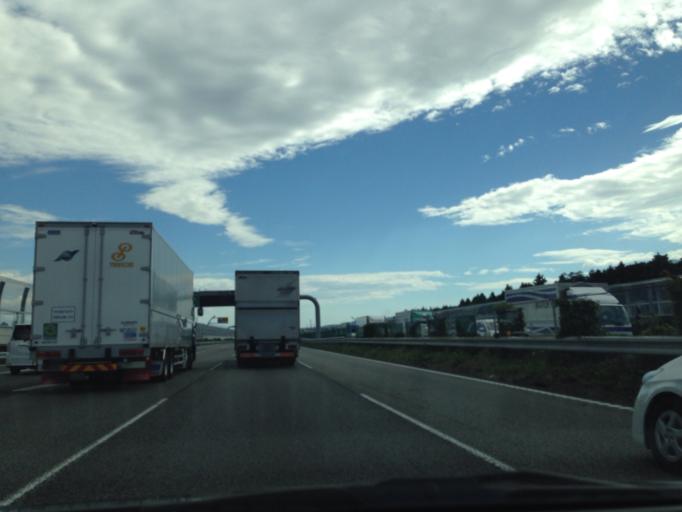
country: JP
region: Shizuoka
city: Gotemba
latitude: 35.2733
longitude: 138.9174
